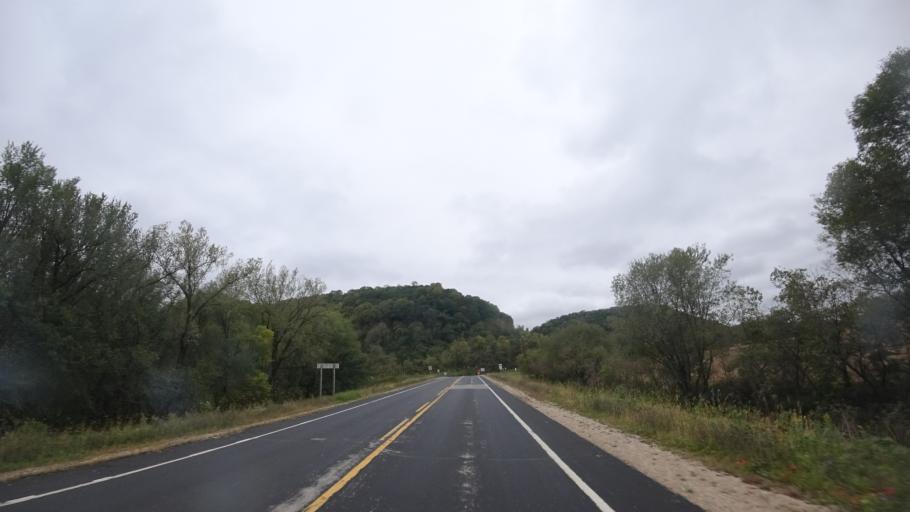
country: US
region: Wisconsin
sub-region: Grant County
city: Boscobel
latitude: 43.1687
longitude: -90.7038
